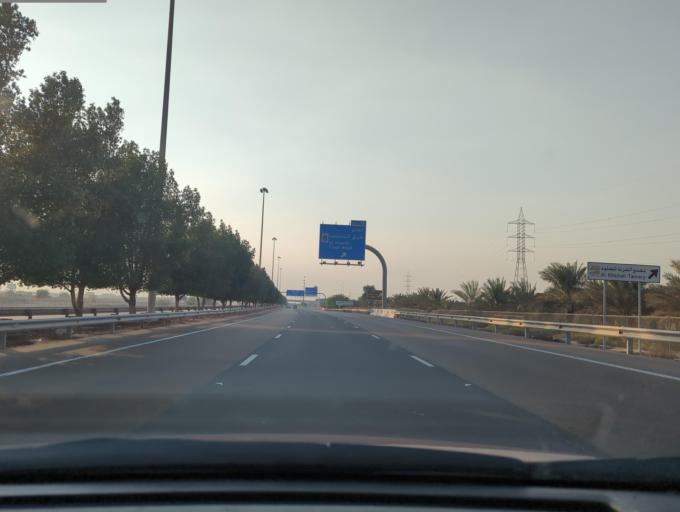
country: AE
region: Abu Dhabi
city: Abu Dhabi
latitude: 24.1904
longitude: 55.0124
